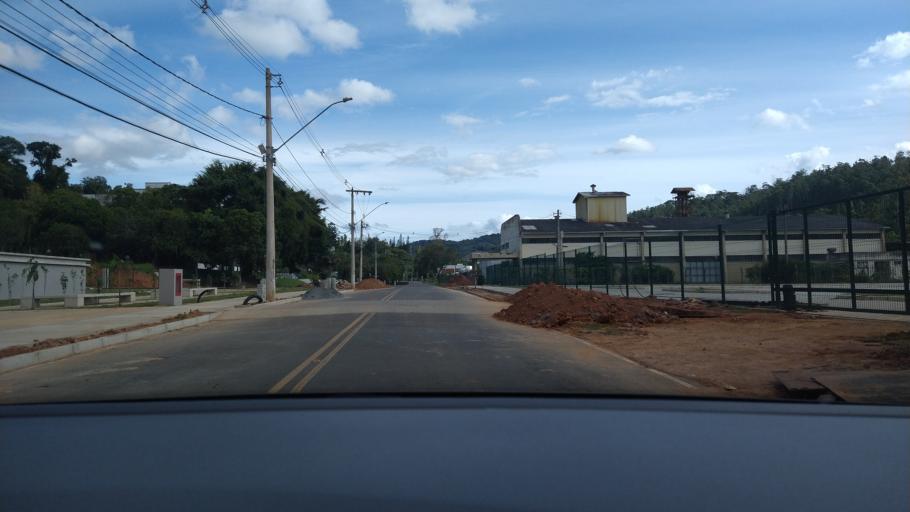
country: BR
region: Minas Gerais
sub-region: Vicosa
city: Vicosa
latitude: -20.7696
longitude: -42.8718
